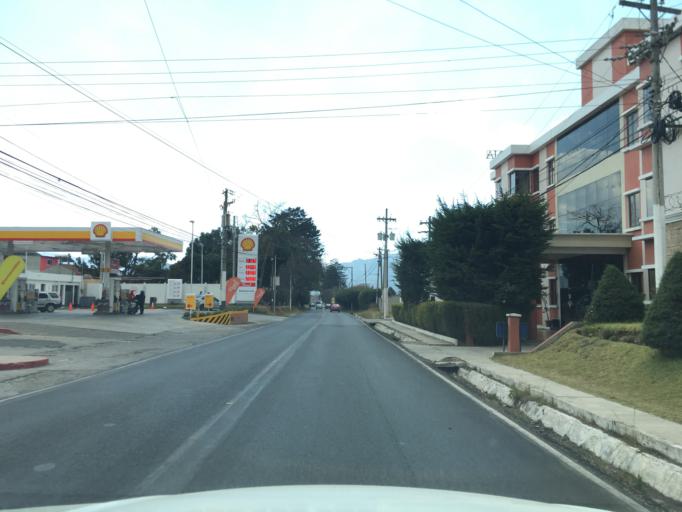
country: GT
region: Quetzaltenango
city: Olintepeque
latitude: 14.8724
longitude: -91.5133
